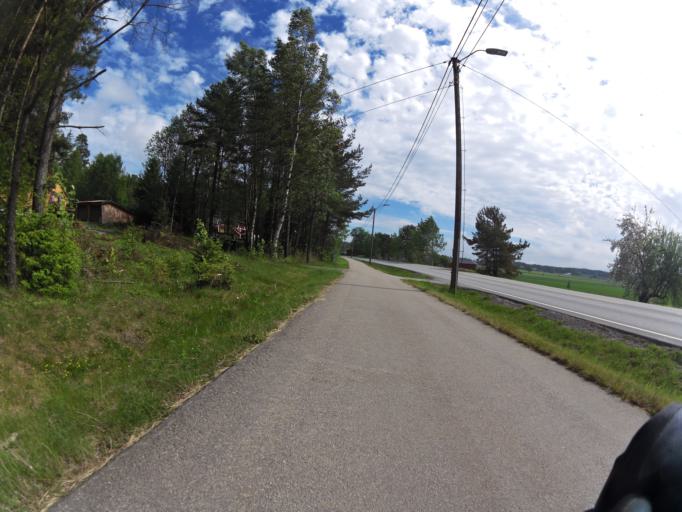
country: NO
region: Ostfold
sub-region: Rade
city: Karlshus
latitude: 59.3598
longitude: 10.8274
